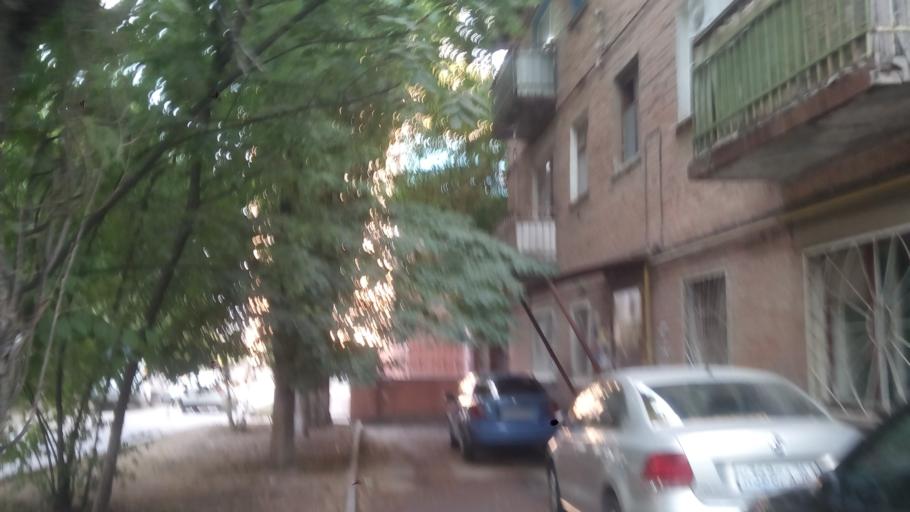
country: RU
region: Rostov
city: Imeni Chkalova
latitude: 47.2582
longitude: 39.7729
